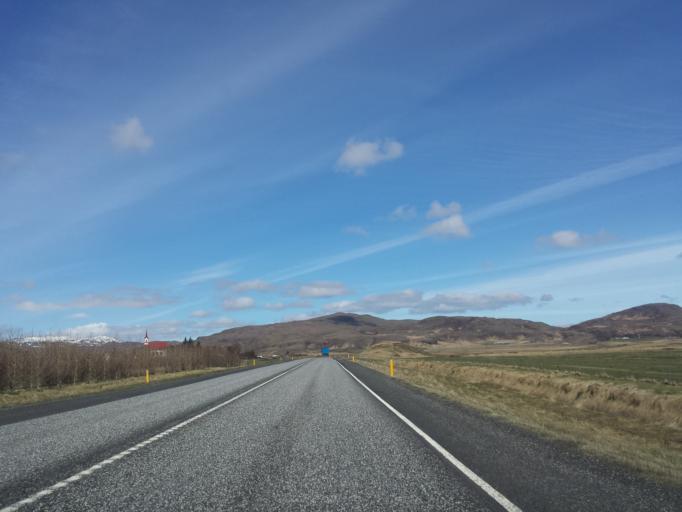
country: IS
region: South
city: Hveragerdi
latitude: 63.9681
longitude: -21.1363
